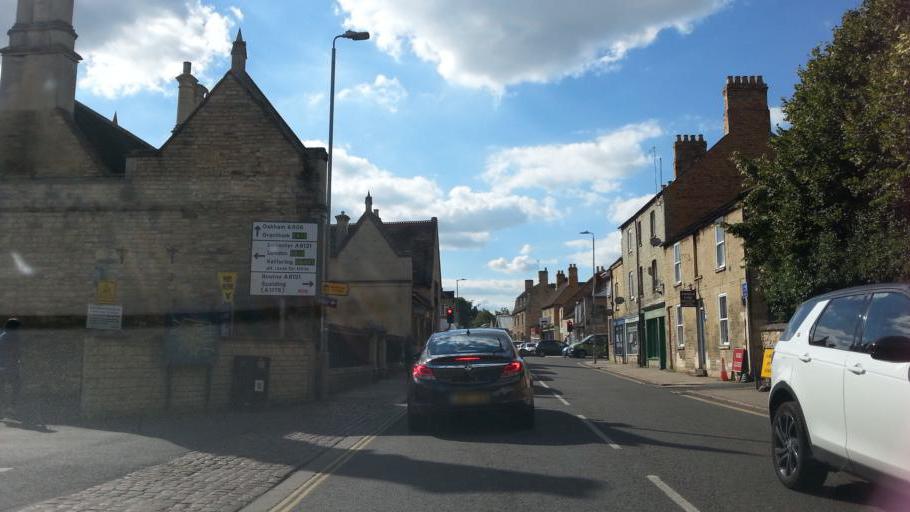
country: GB
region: England
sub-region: Lincolnshire
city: Stamford
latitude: 52.6526
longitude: -0.4830
